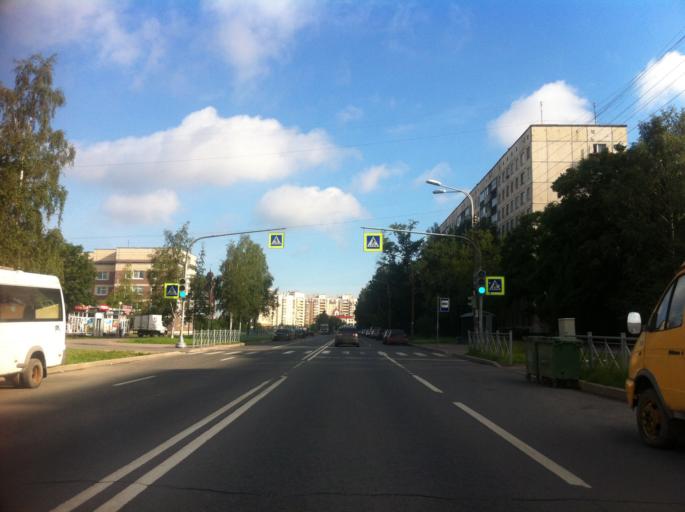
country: RU
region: St.-Petersburg
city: Dachnoye
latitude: 59.8368
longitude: 30.2159
